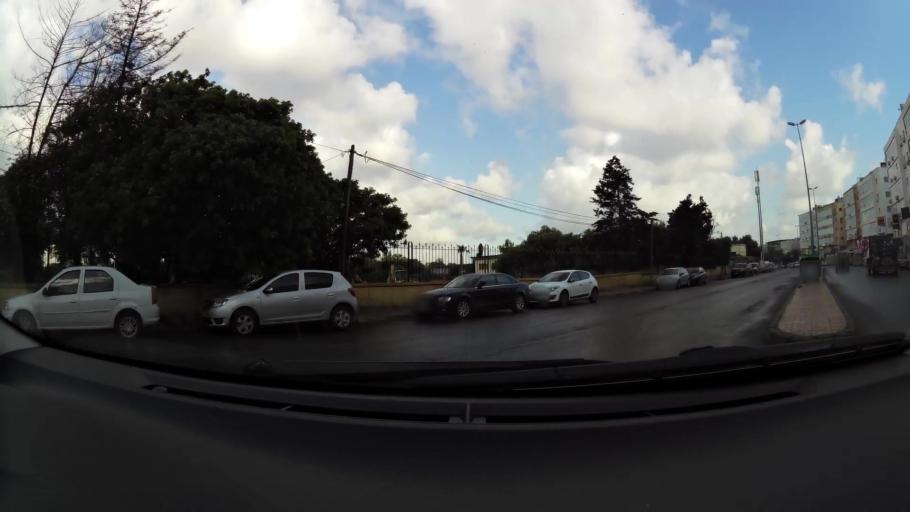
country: MA
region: Grand Casablanca
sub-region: Mediouna
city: Tit Mellil
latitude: 33.5986
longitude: -7.5249
